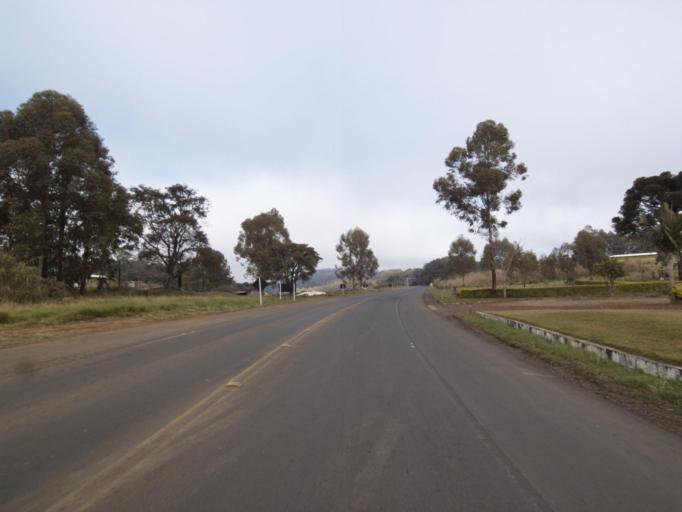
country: BR
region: Rio Grande do Sul
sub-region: Frederico Westphalen
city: Frederico Westphalen
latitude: -27.1040
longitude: -53.2124
